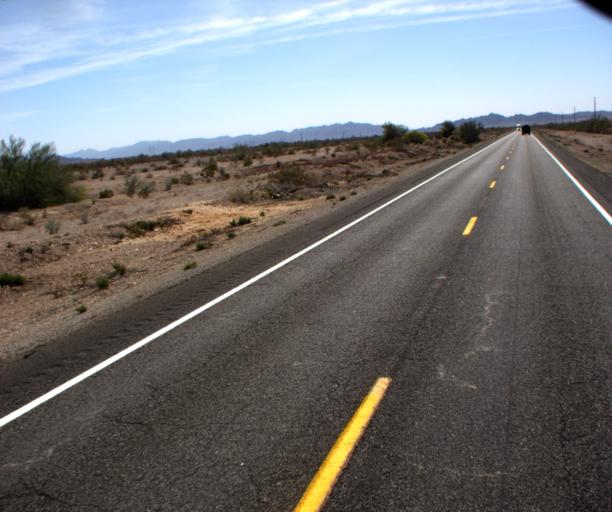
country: US
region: Arizona
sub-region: Yuma County
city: Fortuna Foothills
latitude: 32.8847
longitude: -114.3441
